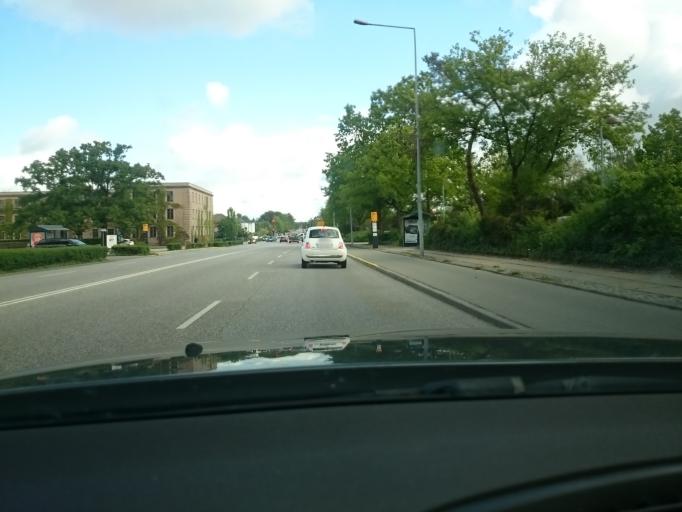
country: DK
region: Capital Region
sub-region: Gentofte Kommune
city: Charlottenlund
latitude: 55.7487
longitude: 12.5575
